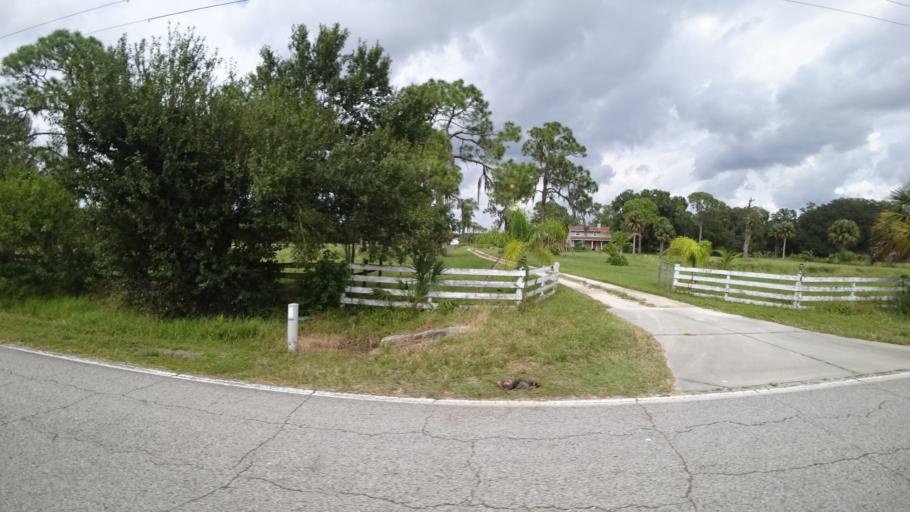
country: US
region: Florida
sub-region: Manatee County
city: Ellenton
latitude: 27.4878
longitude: -82.3845
